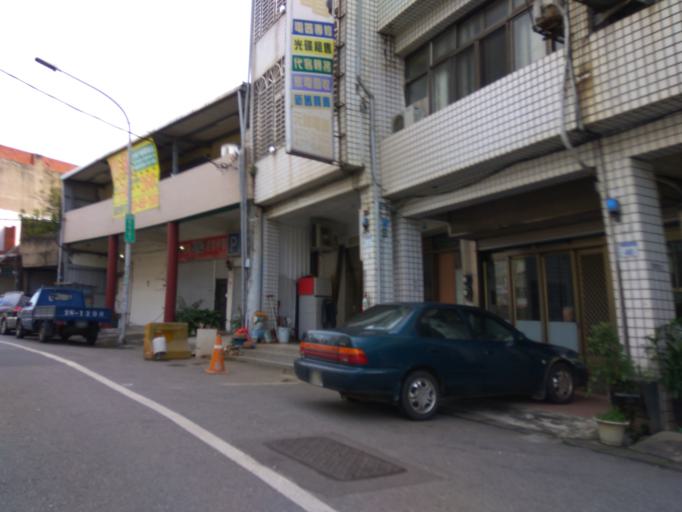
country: TW
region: Taiwan
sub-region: Hsinchu
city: Zhubei
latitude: 24.9716
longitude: 121.1028
